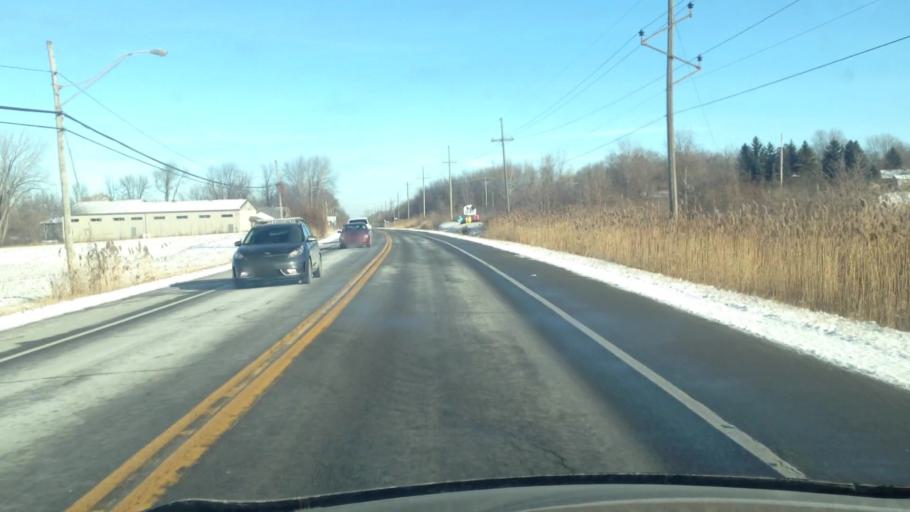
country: CA
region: Quebec
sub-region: Monteregie
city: Beauharnois
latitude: 45.3277
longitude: -73.8241
